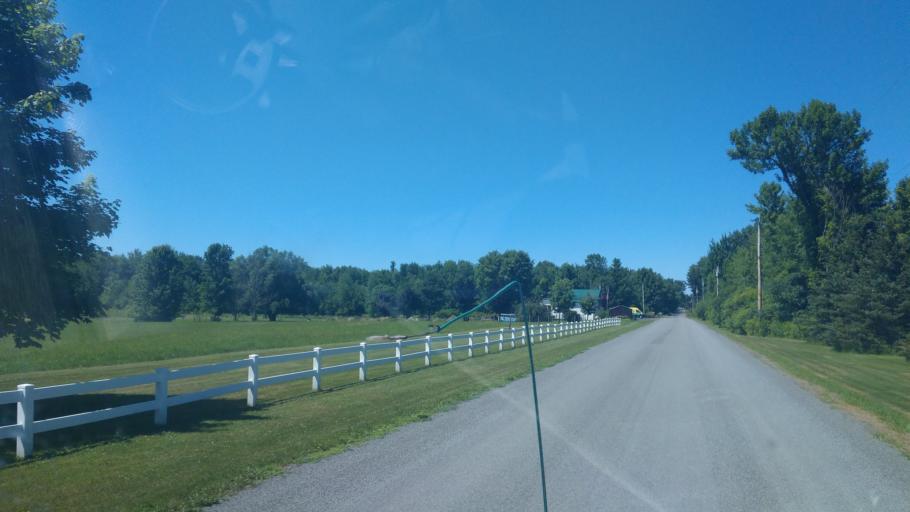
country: US
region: New York
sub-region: Wayne County
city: Sodus
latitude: 43.1771
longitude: -76.9782
